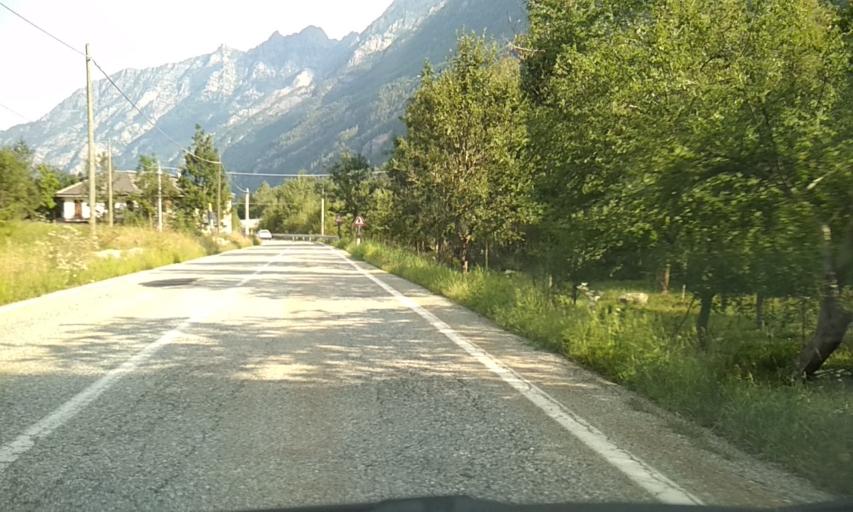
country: IT
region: Piedmont
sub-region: Provincia di Torino
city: Noasca
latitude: 45.4445
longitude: 7.3338
